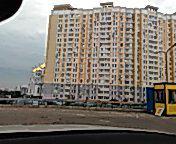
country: RU
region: Moscow
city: Strogino
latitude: 55.8571
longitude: 37.3925
